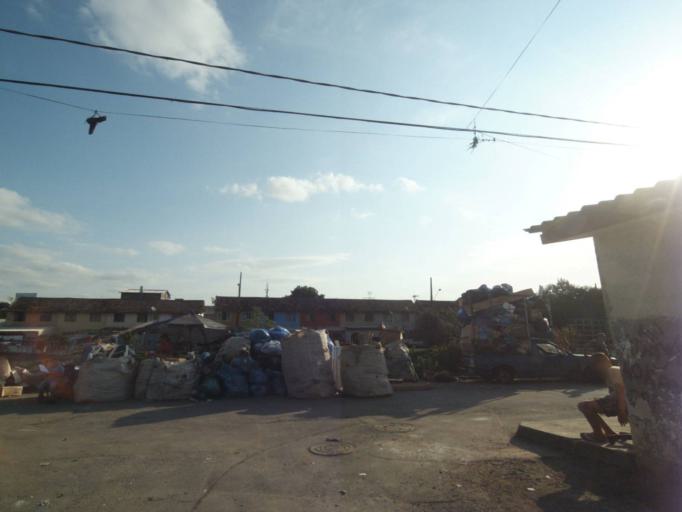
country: BR
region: Parana
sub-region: Curitiba
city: Curitiba
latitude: -25.4446
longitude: -49.2513
